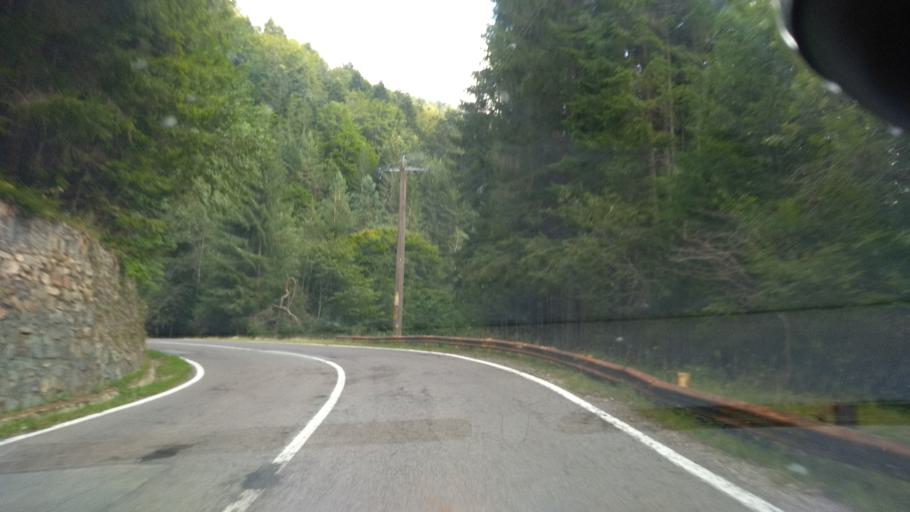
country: RO
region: Arges
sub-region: Comuna Arefu
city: Arefu
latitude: 45.4761
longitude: 24.5999
